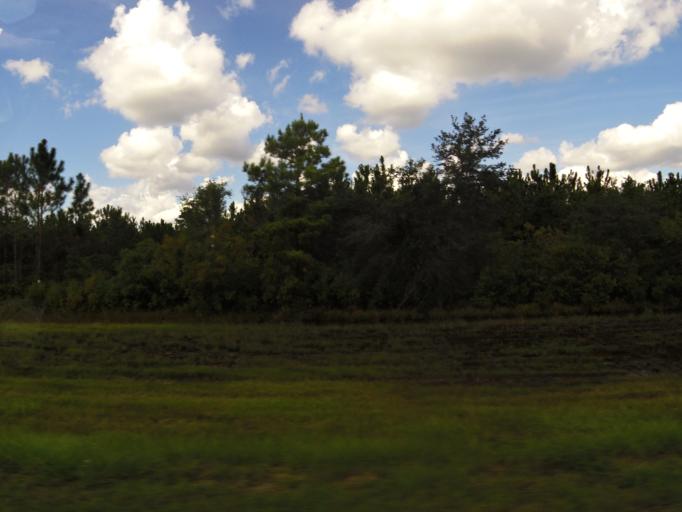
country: US
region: Florida
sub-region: Hamilton County
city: Jasper
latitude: 30.6778
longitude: -82.7071
